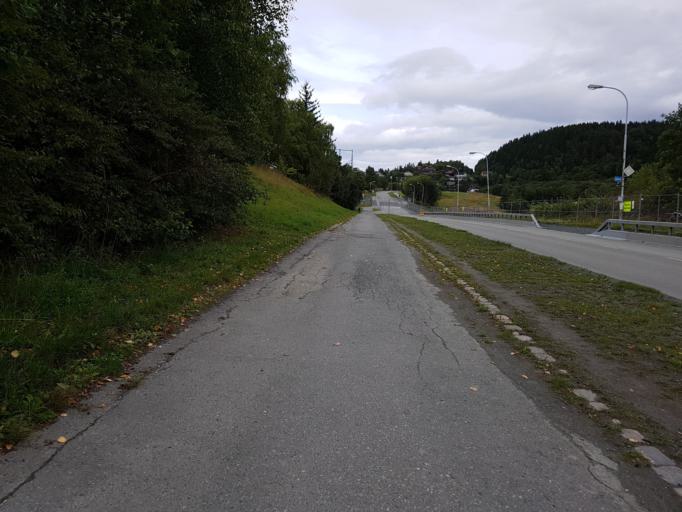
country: NO
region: Sor-Trondelag
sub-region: Trondheim
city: Trondheim
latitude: 63.3923
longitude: 10.4366
